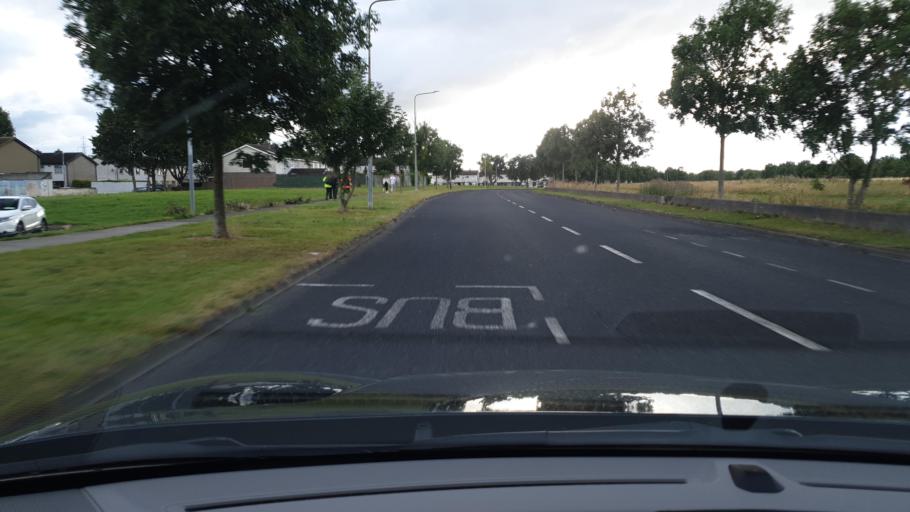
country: IE
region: Leinster
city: Clondalkin
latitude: 53.3286
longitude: -6.4138
